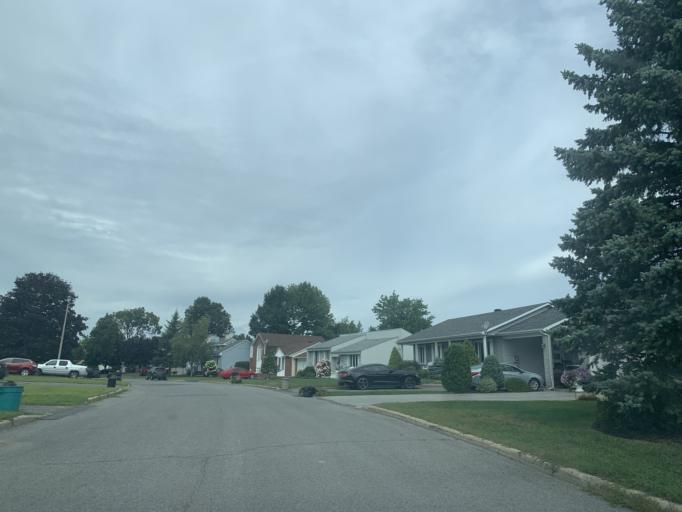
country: CA
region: Ontario
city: Hawkesbury
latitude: 45.5982
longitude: -74.6000
